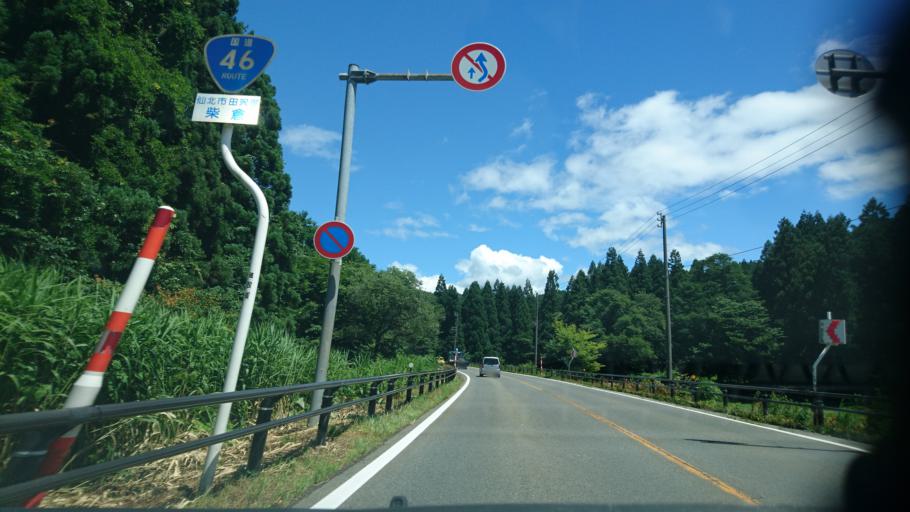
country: JP
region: Akita
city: Kakunodatemachi
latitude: 39.6544
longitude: 140.6722
